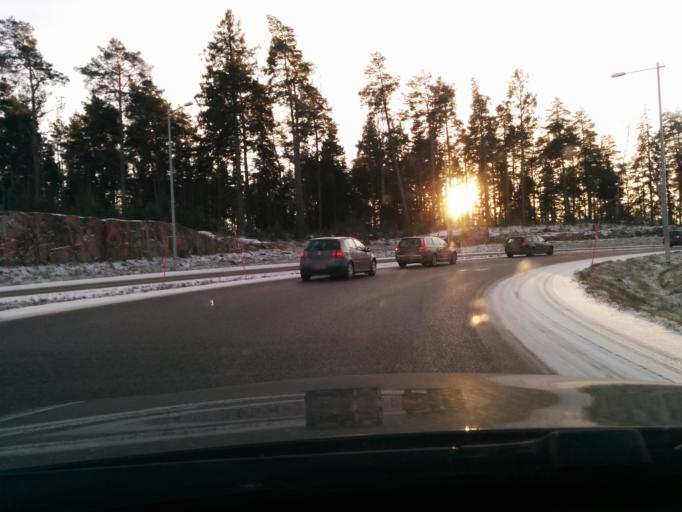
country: SE
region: Stockholm
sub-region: Taby Kommun
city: Taby
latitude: 59.4751
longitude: 18.0535
